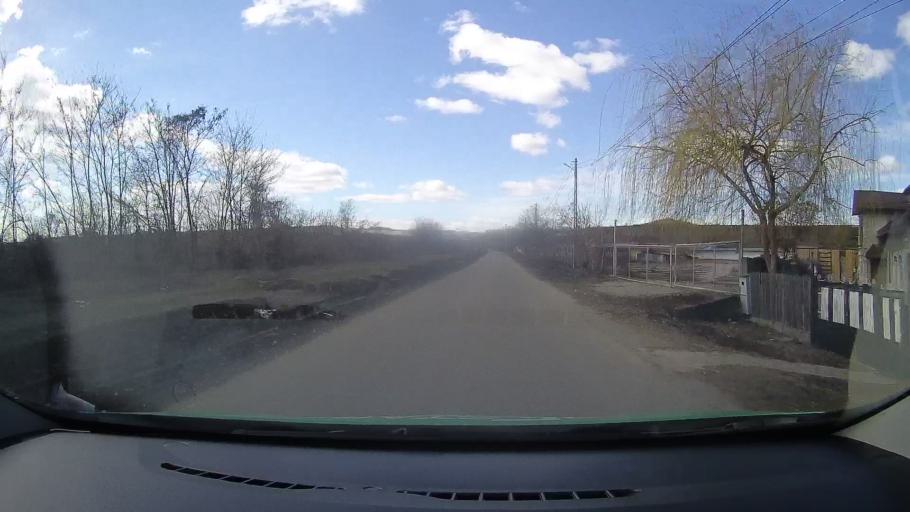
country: RO
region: Dambovita
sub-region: Comuna Doicesti
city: Doicesti
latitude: 44.9960
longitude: 25.3921
